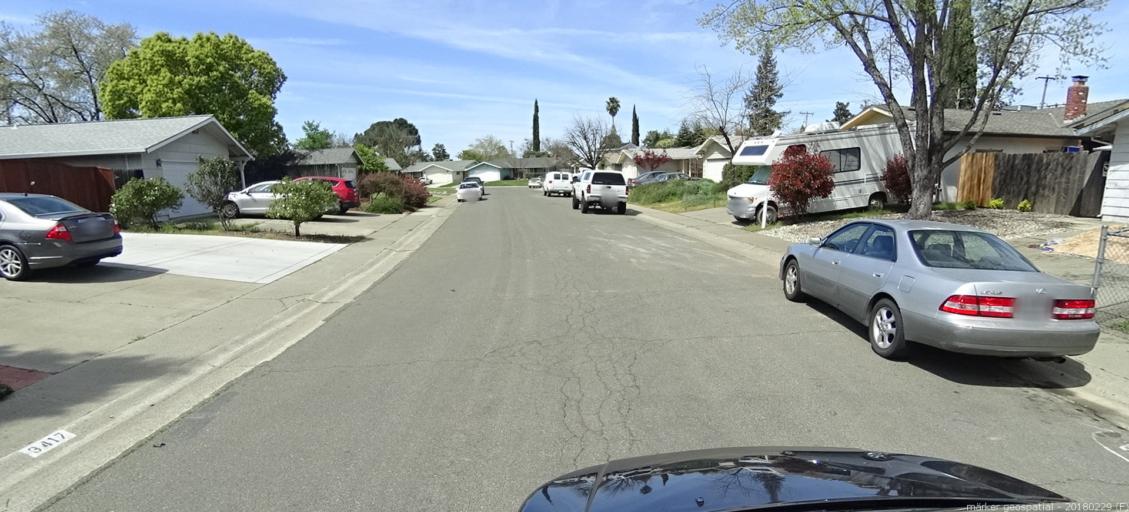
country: US
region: California
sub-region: Sacramento County
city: Rosemont
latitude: 38.5503
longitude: -121.3589
